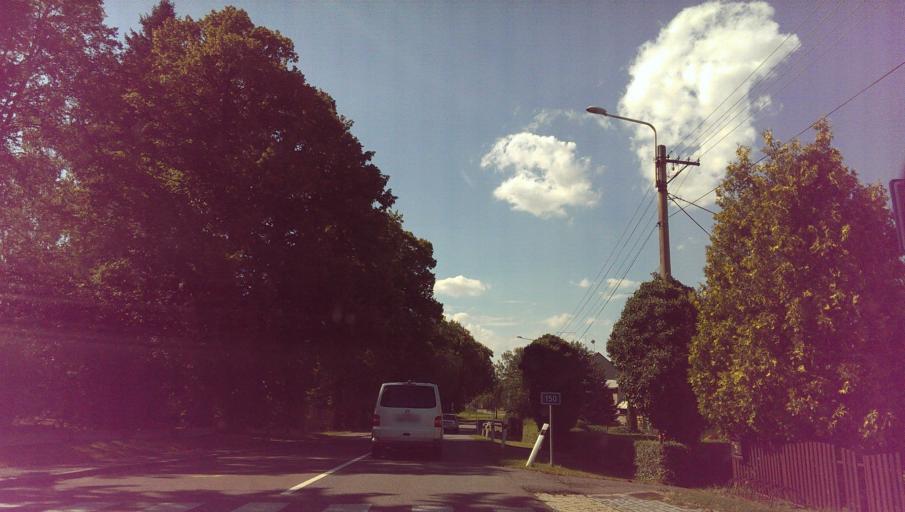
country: CZ
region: Zlin
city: Kelc
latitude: 49.4405
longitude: 17.8313
